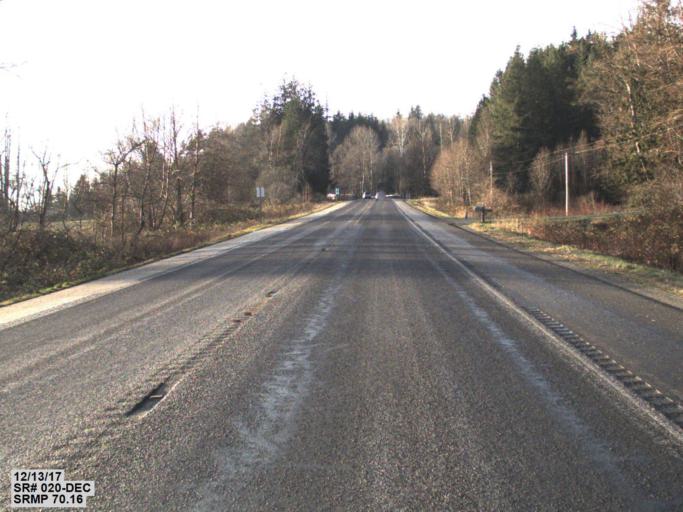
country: US
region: Washington
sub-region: Skagit County
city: Sedro-Woolley
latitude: 48.5308
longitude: -122.1453
